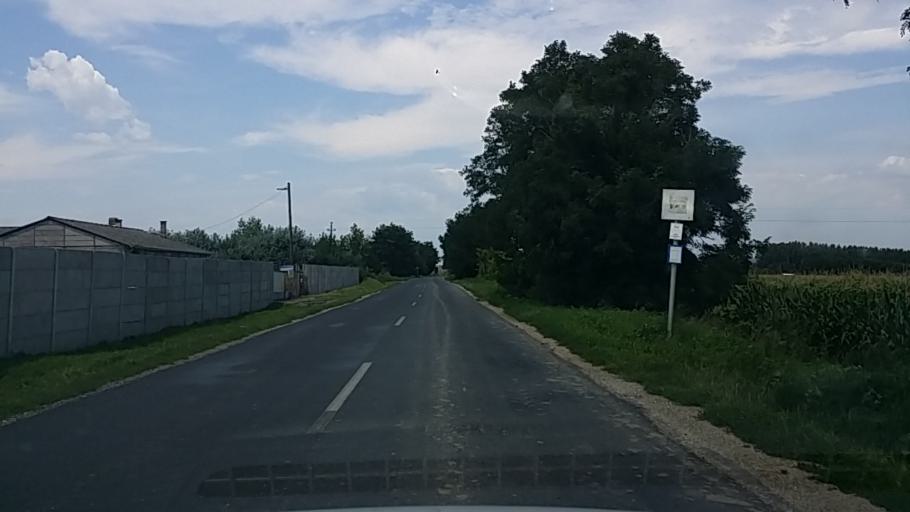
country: HU
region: Zala
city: Nagykanizsa
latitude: 46.4418
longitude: 16.9546
